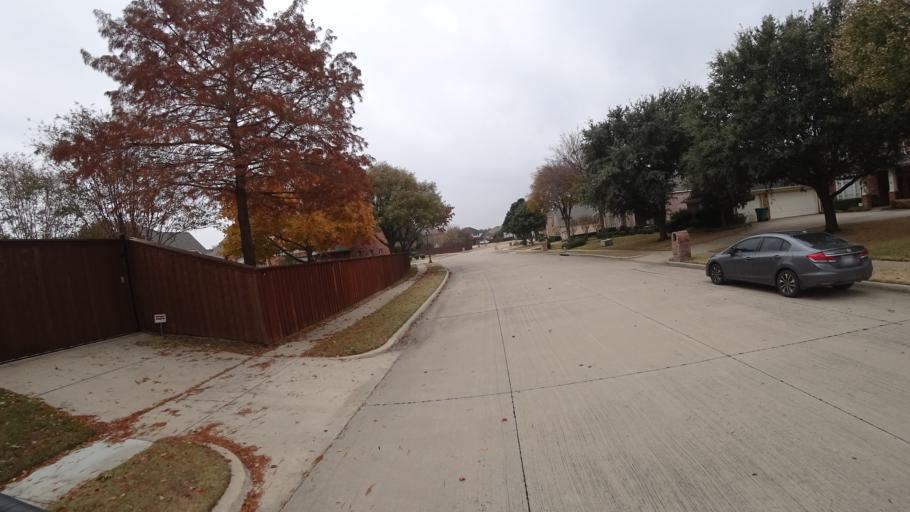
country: US
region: Texas
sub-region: Denton County
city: Lewisville
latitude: 33.0330
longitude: -96.9387
